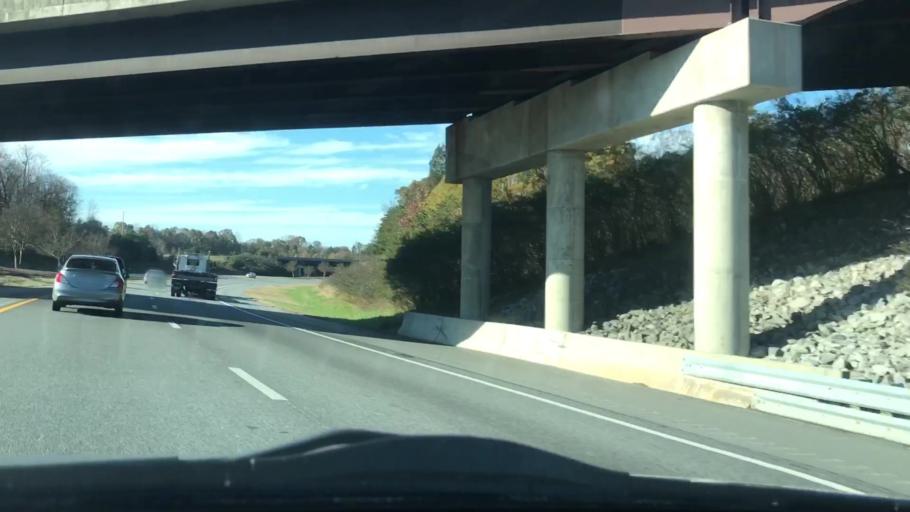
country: US
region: North Carolina
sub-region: Guilford County
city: High Point
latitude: 36.0074
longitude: -80.0310
